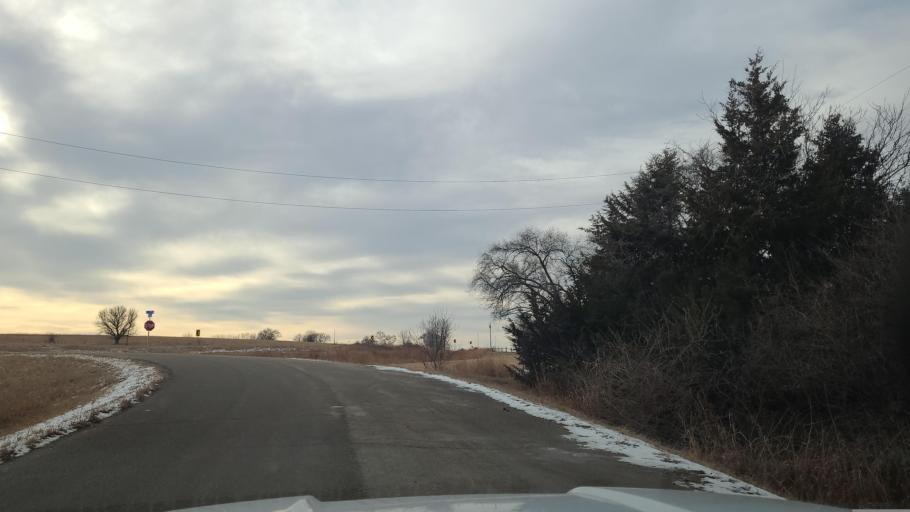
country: US
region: Kansas
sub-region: Shawnee County
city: Topeka
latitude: 39.0418
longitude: -95.4641
